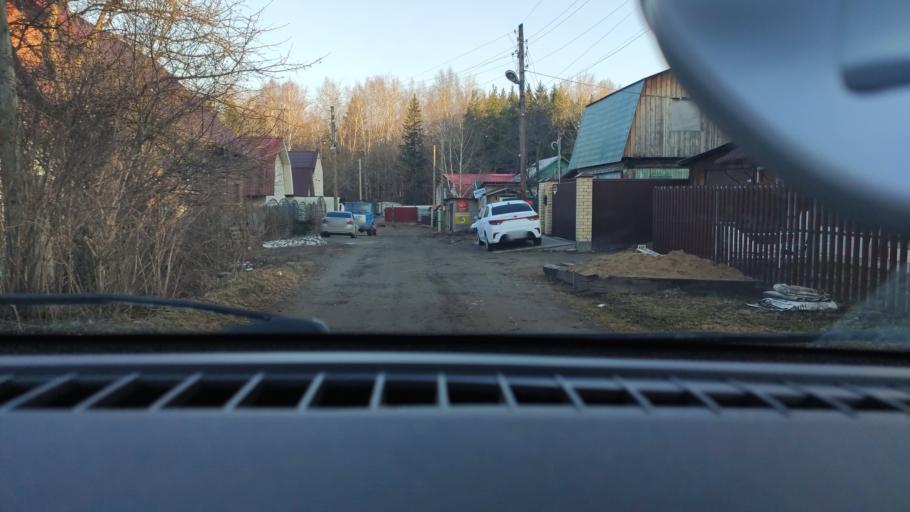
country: RU
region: Perm
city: Kondratovo
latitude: 57.9672
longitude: 56.1434
